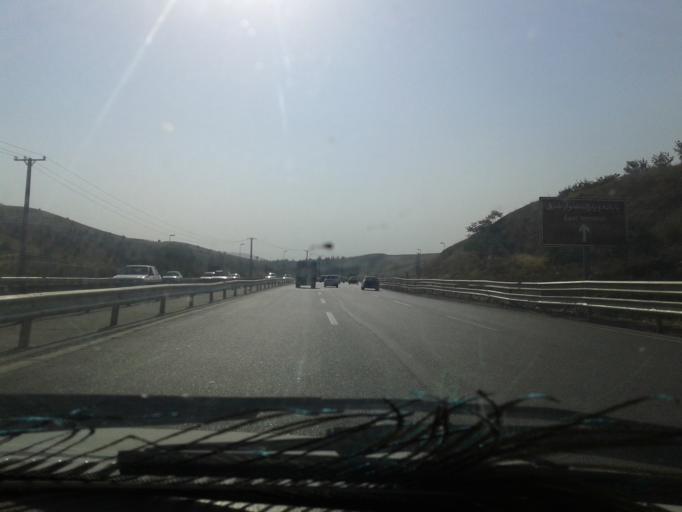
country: IR
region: Tehran
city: Tehran
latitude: 35.7303
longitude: 51.6328
